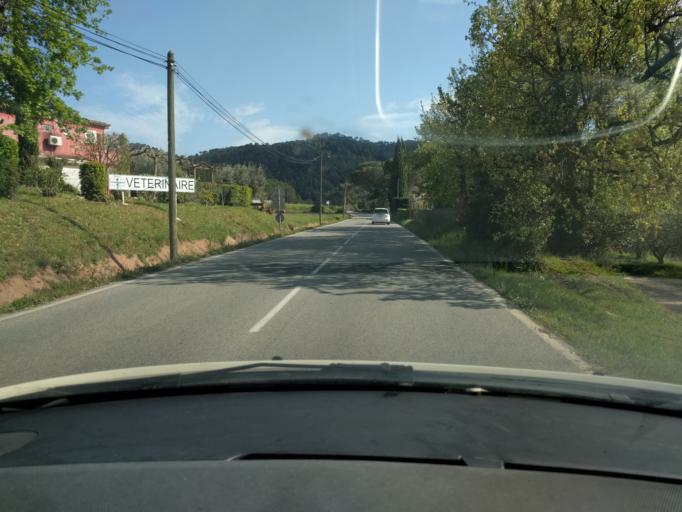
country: FR
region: Provence-Alpes-Cote d'Azur
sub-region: Departement du Var
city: Pierrefeu-du-Var
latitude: 43.2204
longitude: 6.1431
